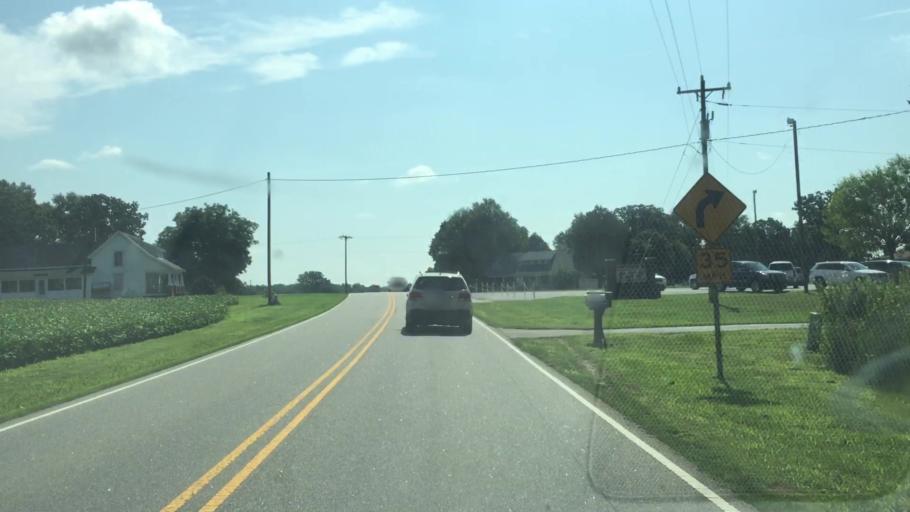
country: US
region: North Carolina
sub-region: Anson County
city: Burnsville
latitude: 35.1045
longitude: -80.3230
